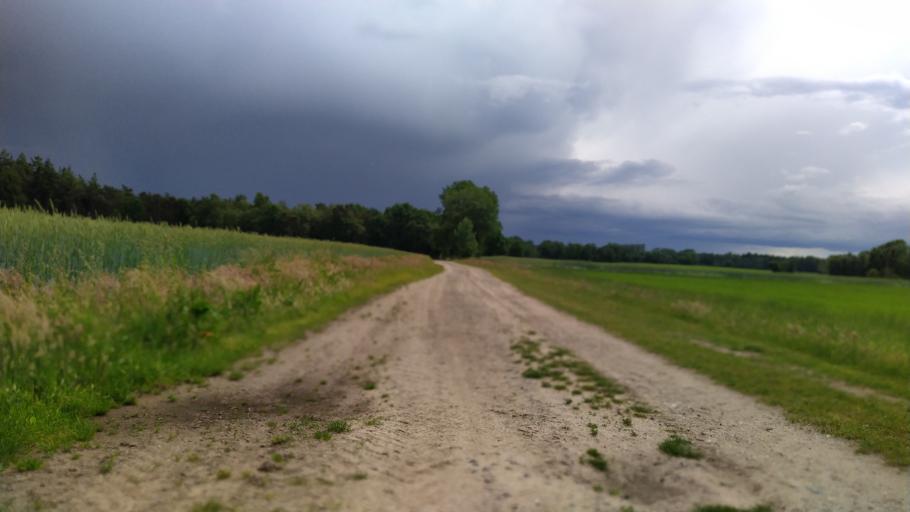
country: DE
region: Lower Saxony
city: Kutenholz
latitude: 53.4593
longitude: 9.3454
